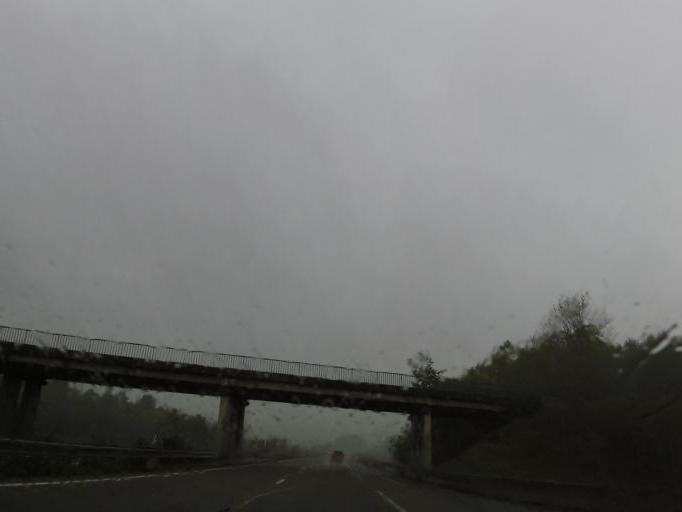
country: FR
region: Picardie
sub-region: Departement de l'Aisne
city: Montreuil-aux-Lions
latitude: 49.0413
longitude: 3.2468
